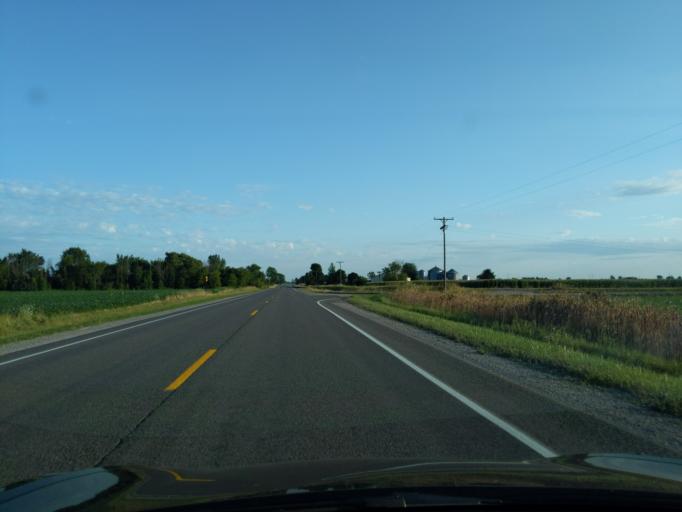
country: US
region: Michigan
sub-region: Gratiot County
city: Breckenridge
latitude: 43.5102
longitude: -84.3698
